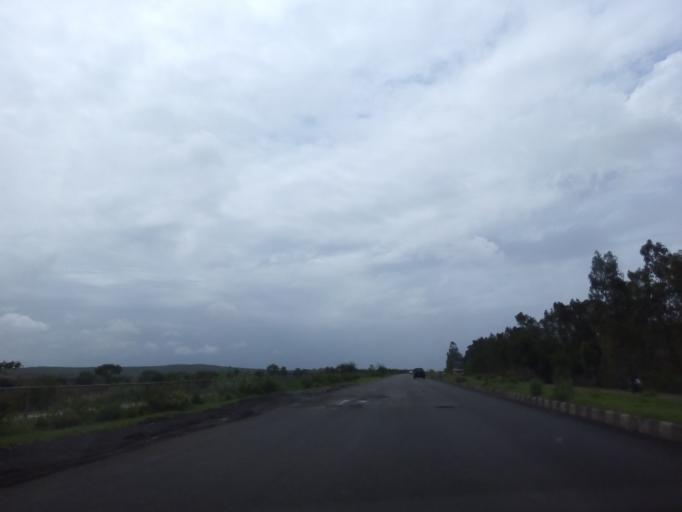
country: IN
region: Karnataka
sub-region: Haveri
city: Byadgi
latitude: 14.7107
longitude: 75.5076
